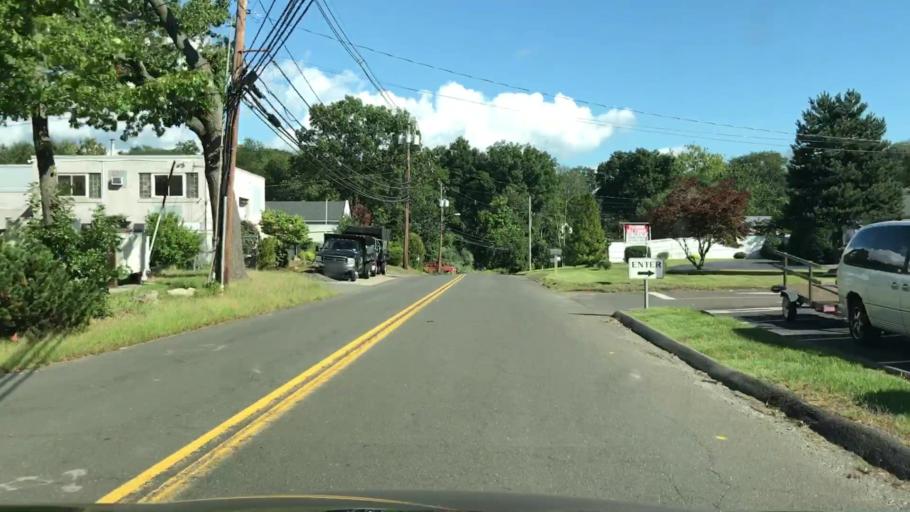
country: US
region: Connecticut
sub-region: New Haven County
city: Wallingford Center
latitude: 41.4333
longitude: -72.8345
